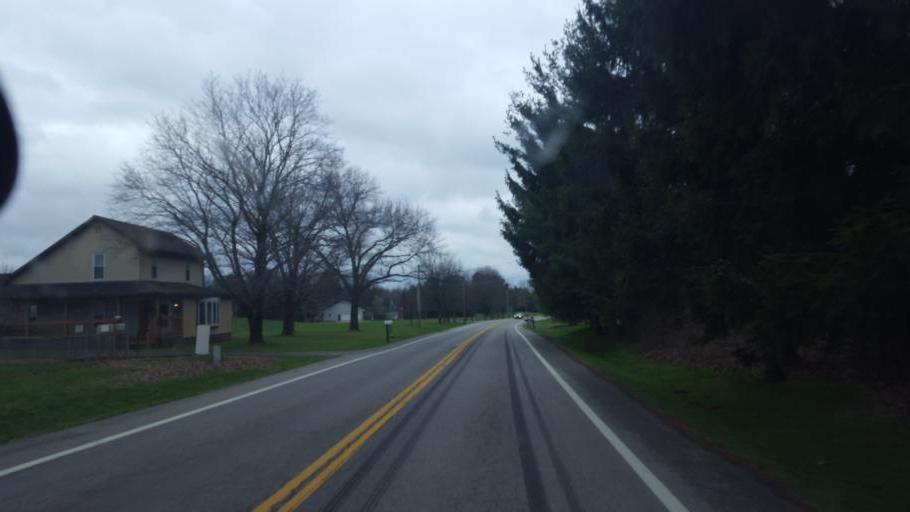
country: US
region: Ohio
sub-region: Delaware County
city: Sunbury
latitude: 40.2686
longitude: -82.8532
